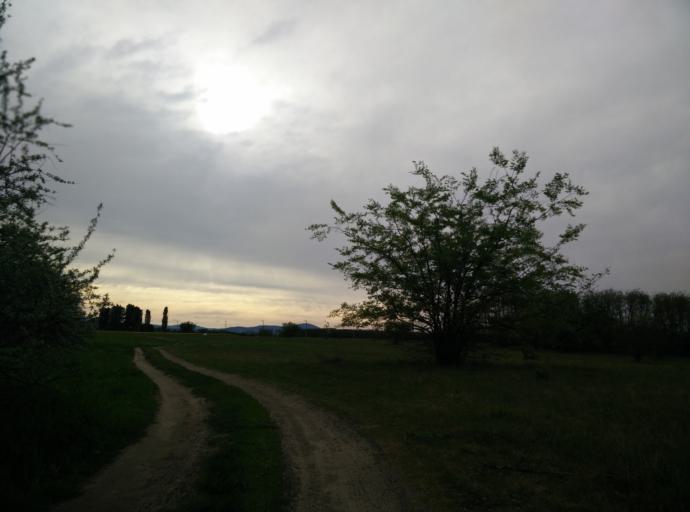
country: HU
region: Pest
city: Fot
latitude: 47.6079
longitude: 19.1694
